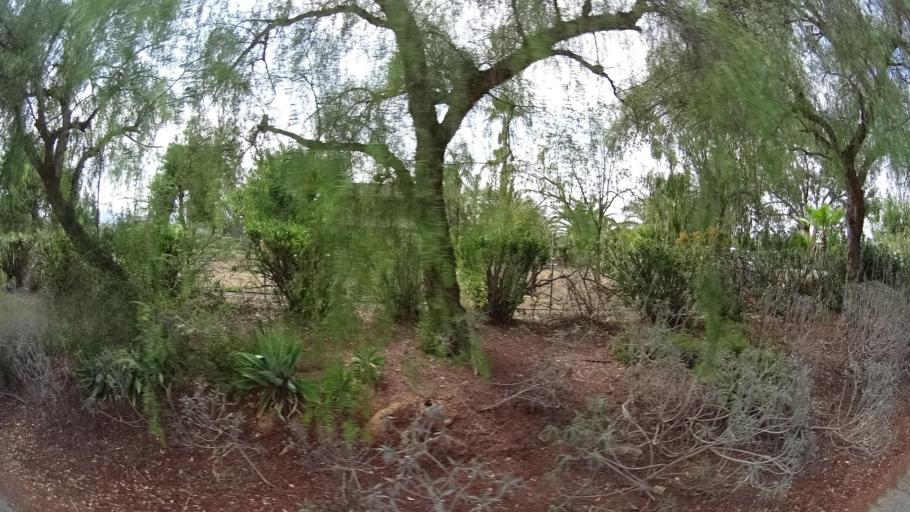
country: US
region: California
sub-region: San Diego County
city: Ramona
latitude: 33.0307
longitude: -116.8450
